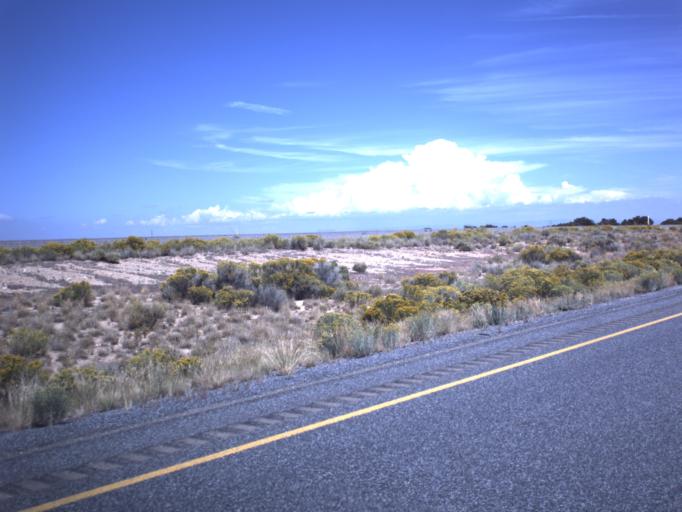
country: US
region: Utah
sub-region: Emery County
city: Castle Dale
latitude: 38.8974
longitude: -110.5871
